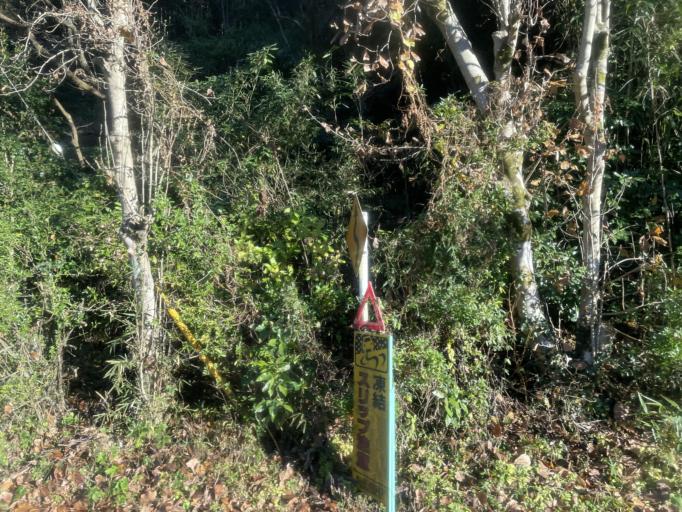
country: JP
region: Saitama
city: Yorii
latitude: 36.0538
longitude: 139.1786
